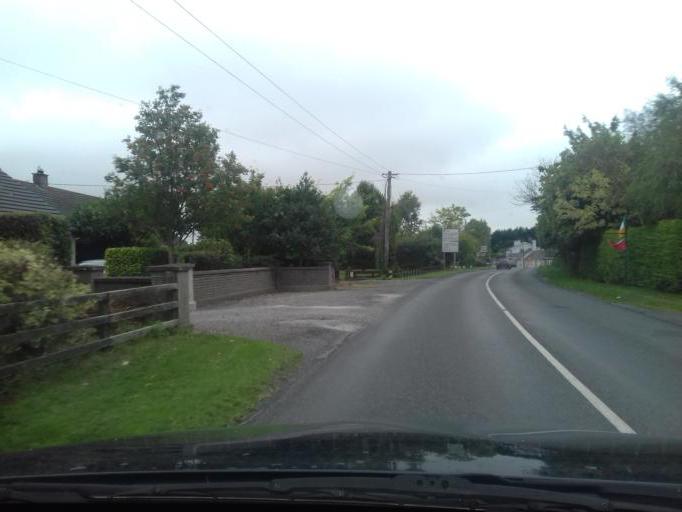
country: IE
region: Leinster
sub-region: County Carlow
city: Bagenalstown
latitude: 52.6926
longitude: -6.9607
